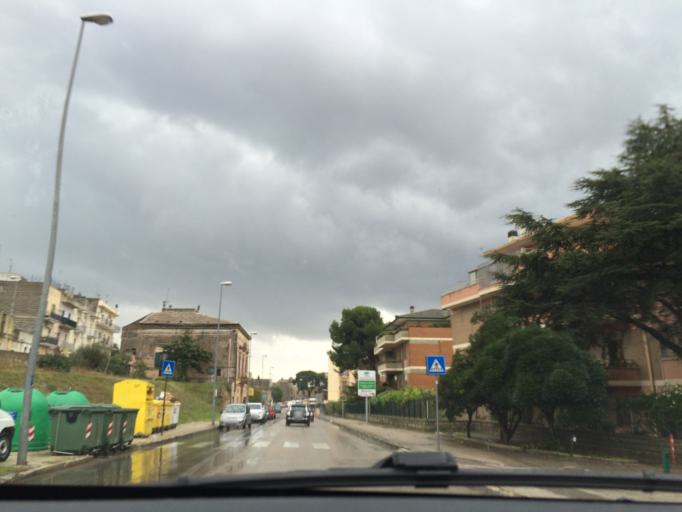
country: IT
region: Basilicate
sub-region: Provincia di Matera
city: Matera
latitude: 40.6552
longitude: 16.6170
